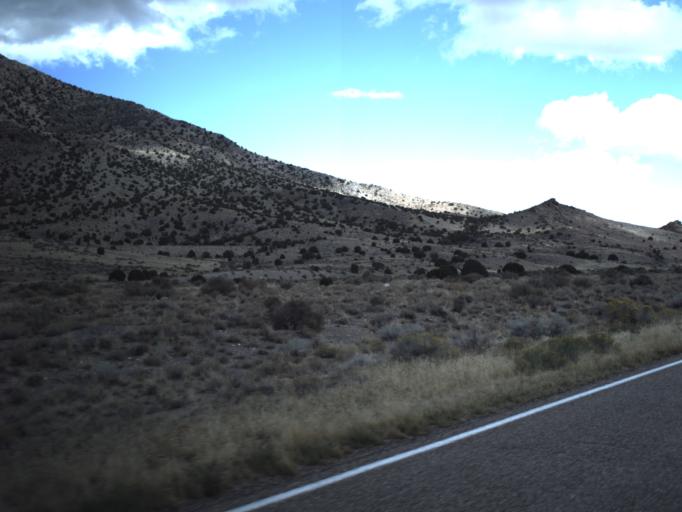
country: US
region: Utah
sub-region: Beaver County
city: Milford
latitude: 38.4350
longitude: -113.2949
